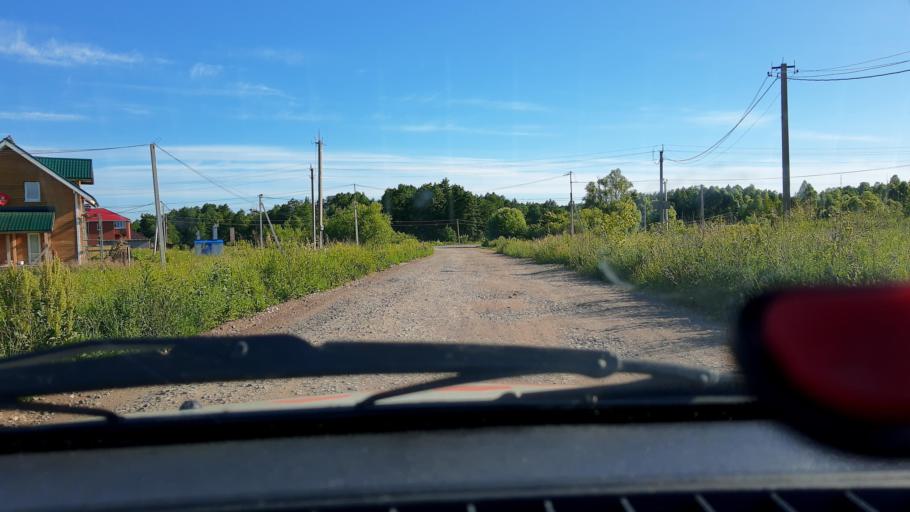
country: RU
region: Bashkortostan
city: Kabakovo
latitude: 54.7458
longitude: 56.2091
